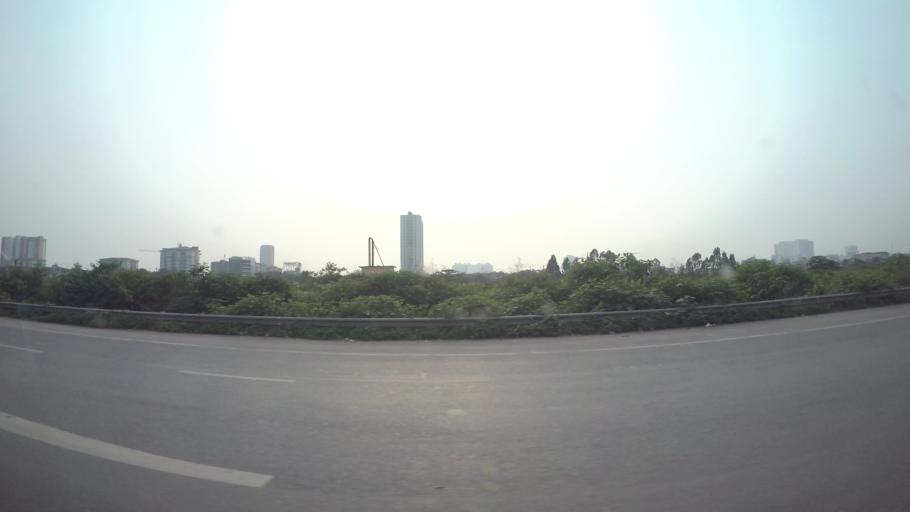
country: VN
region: Ha Noi
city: Van Dien
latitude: 20.9628
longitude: 105.8491
